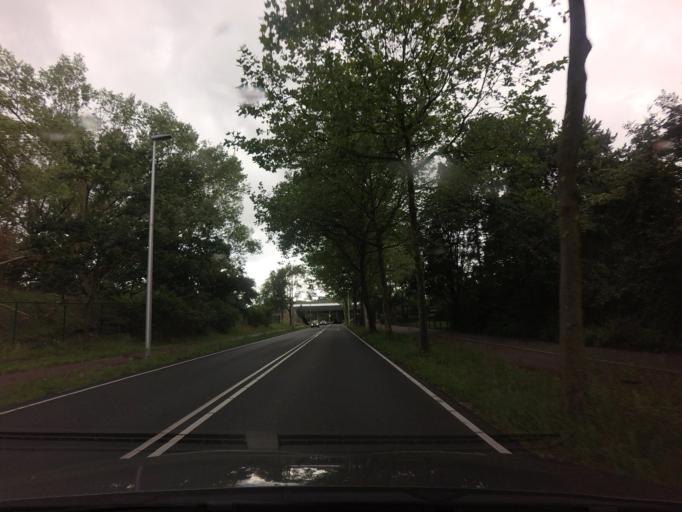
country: NL
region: North Holland
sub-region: Gemeente Zandvoort
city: Zandvoort
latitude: 52.3665
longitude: 4.5656
